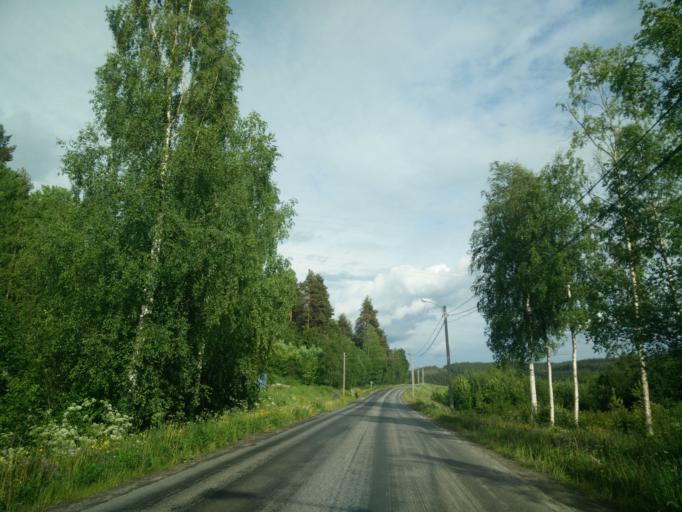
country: SE
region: Vaesternorrland
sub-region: Sundsvalls Kommun
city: Sundsvall
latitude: 62.4390
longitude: 17.2638
